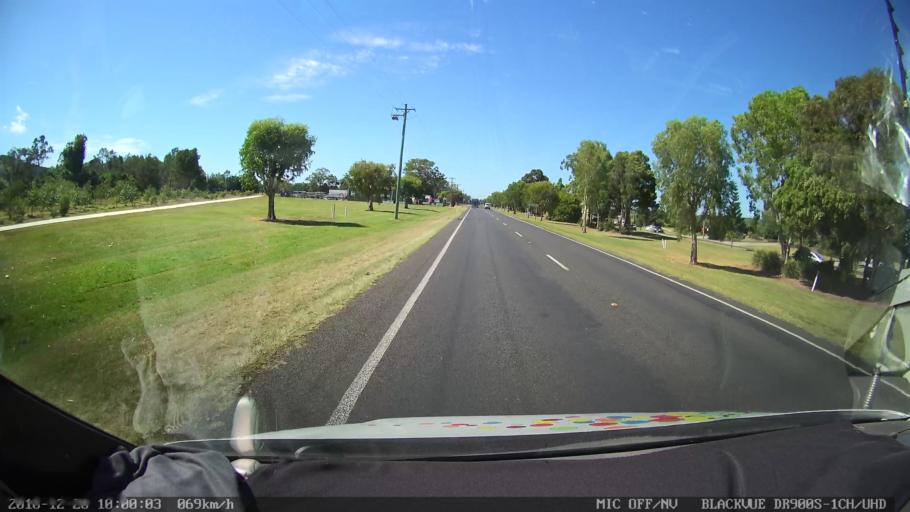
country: AU
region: New South Wales
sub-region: Lismore Municipality
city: Lismore
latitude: -28.8284
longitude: 153.2650
